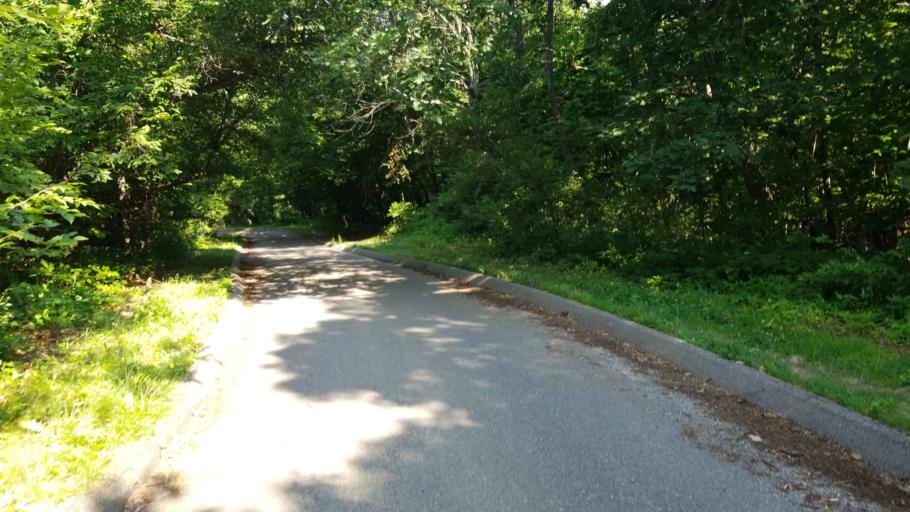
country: US
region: Nebraska
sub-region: Cass County
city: Louisville
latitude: 41.0211
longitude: -96.2451
